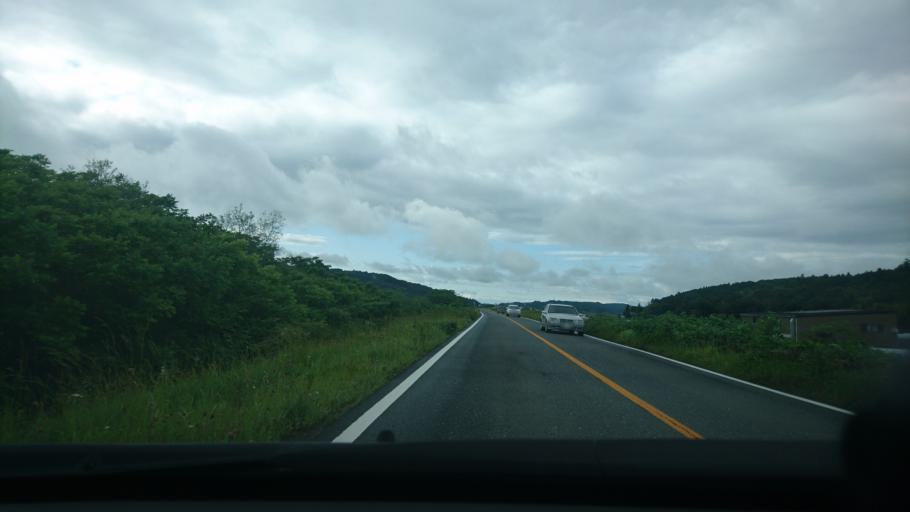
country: JP
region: Miyagi
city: Wakuya
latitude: 38.6292
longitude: 141.2924
